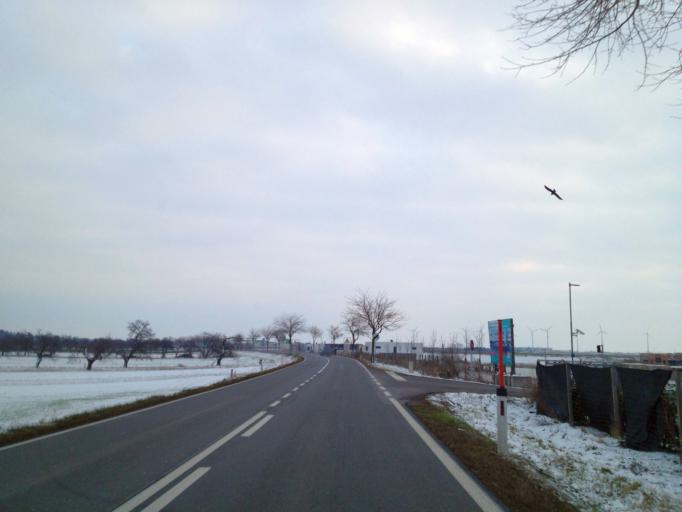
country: AT
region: Lower Austria
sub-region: Politischer Bezirk Bruck an der Leitha
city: Berg
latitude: 48.1022
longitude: 17.0445
